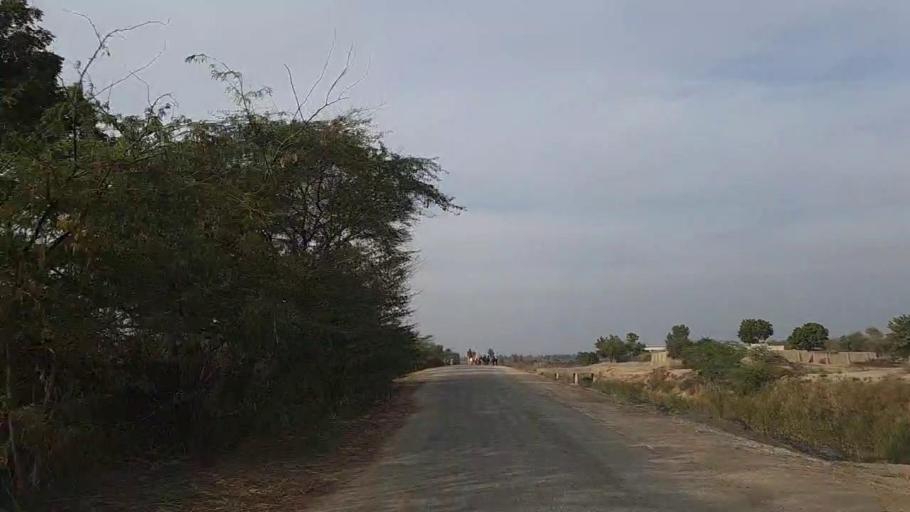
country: PK
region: Sindh
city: Daur
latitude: 26.4823
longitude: 68.4642
